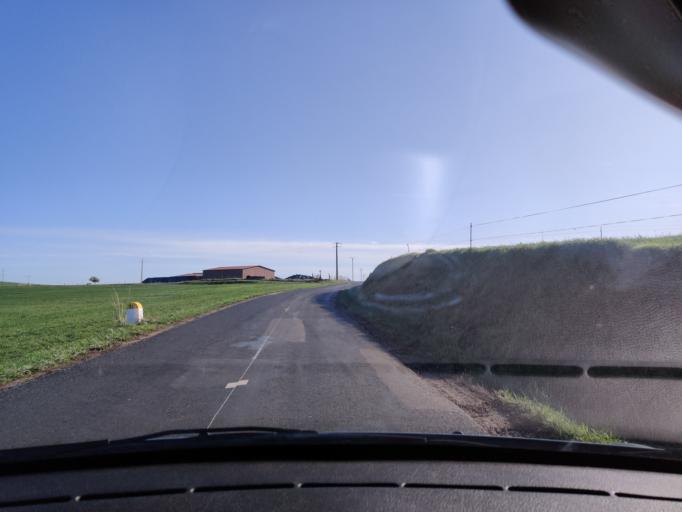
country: FR
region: Auvergne
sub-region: Departement du Puy-de-Dome
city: Aigueperse
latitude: 46.0345
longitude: 3.1604
